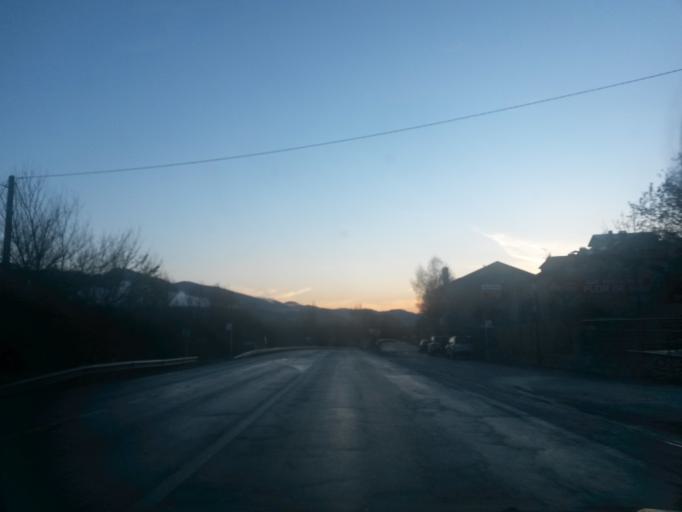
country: ES
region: Catalonia
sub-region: Provincia de Girona
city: Isovol
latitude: 42.3631
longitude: 1.8087
